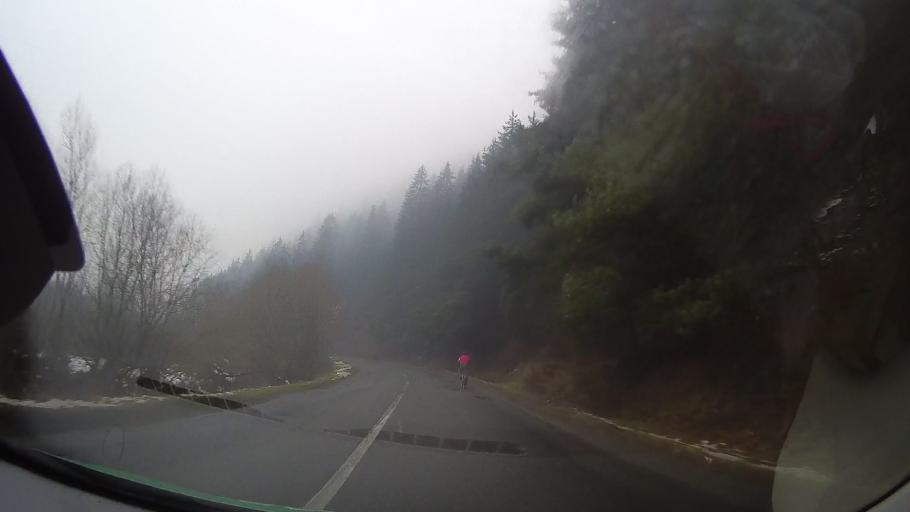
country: RO
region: Harghita
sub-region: Municipiul Gheorgheni
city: Gheorgheni
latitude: 46.7335
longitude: 25.6489
